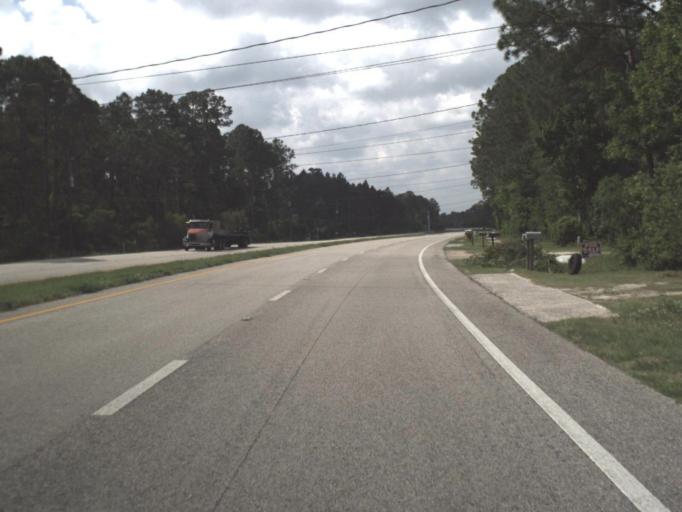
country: US
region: Florida
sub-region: Saint Johns County
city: Butler Beach
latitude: 29.6902
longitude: -81.2946
